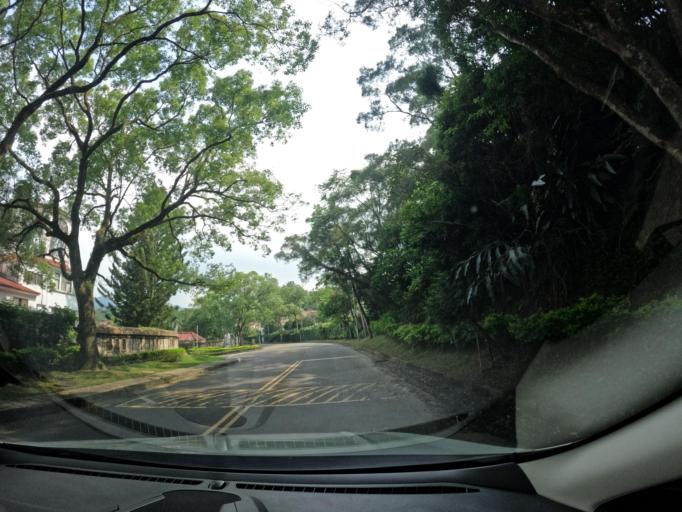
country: TW
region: Taiwan
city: Daxi
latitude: 24.8890
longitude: 121.3222
